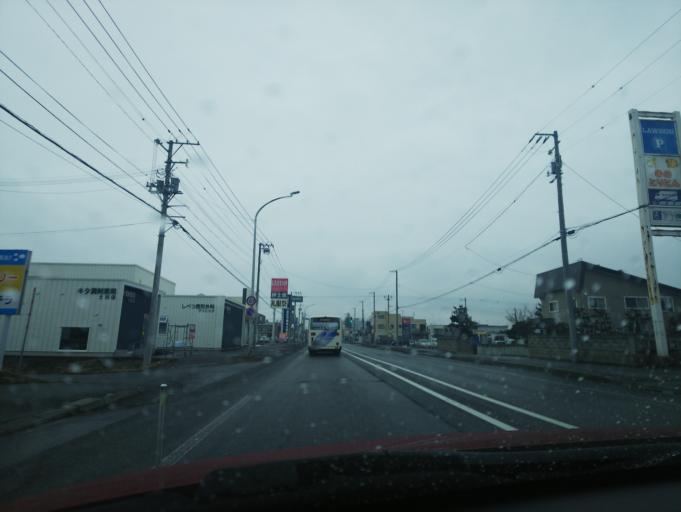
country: JP
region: Hokkaido
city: Nayoro
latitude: 44.1676
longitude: 142.3949
